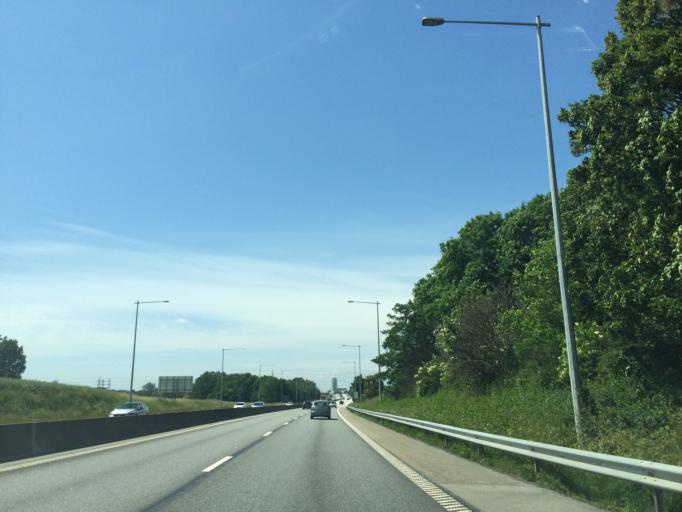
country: SE
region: Skane
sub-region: Burlovs Kommun
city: Arloev
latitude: 55.6247
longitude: 13.0701
